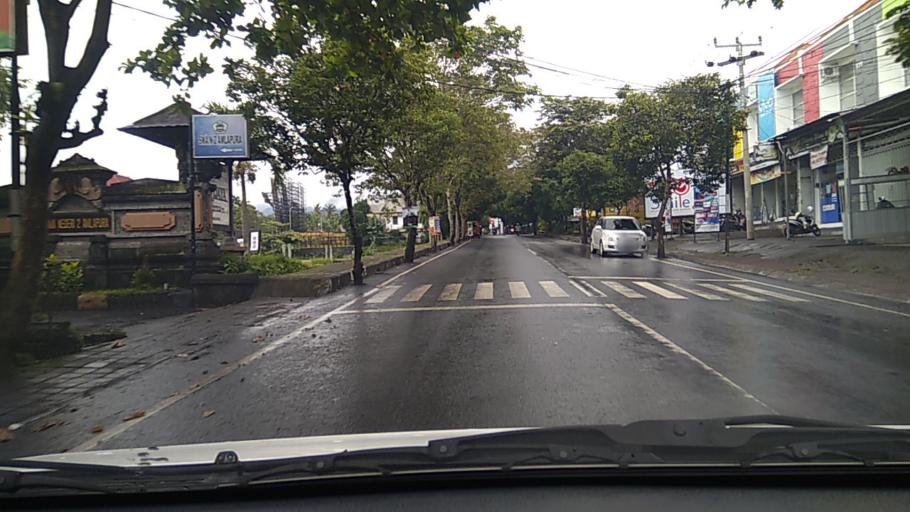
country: ID
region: Bali
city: Subagan
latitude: -8.4434
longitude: 115.6004
